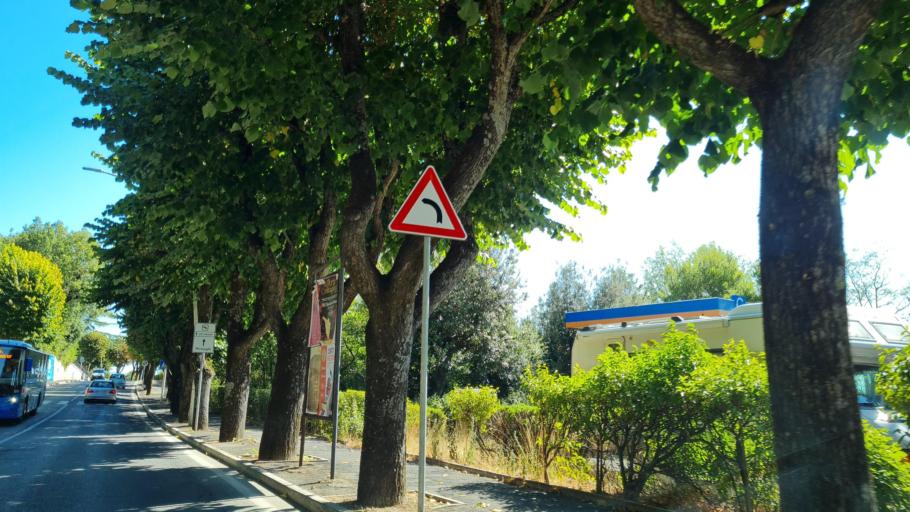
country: IT
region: Tuscany
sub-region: Provincia di Siena
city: Chianciano Terme
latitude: 43.0524
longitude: 11.8217
